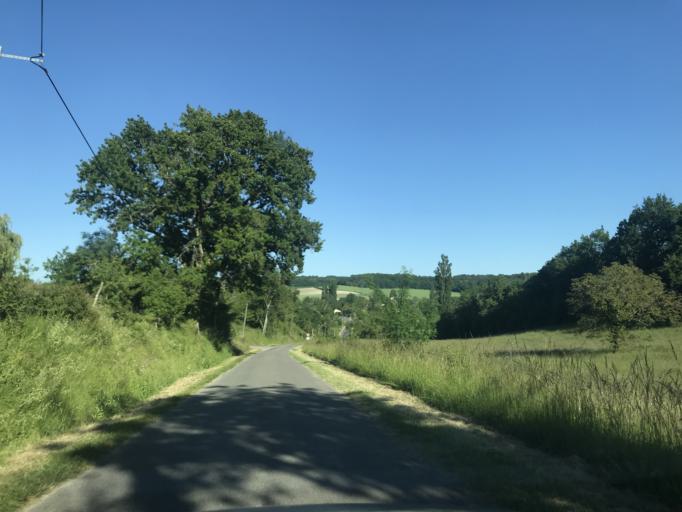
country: FR
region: Poitou-Charentes
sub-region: Departement de la Charente
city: Chalais
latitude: 45.2514
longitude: 0.0283
